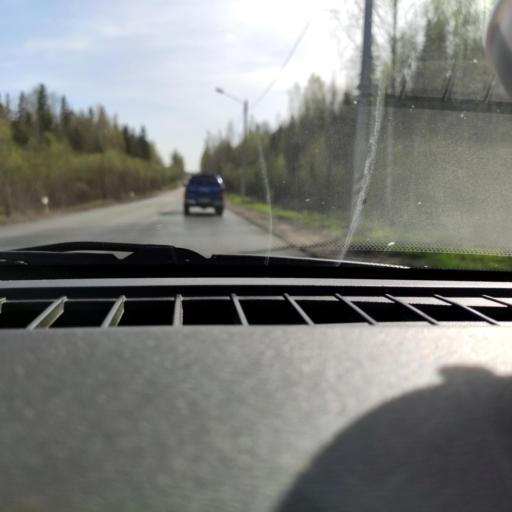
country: RU
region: Perm
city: Perm
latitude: 58.1327
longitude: 56.3015
